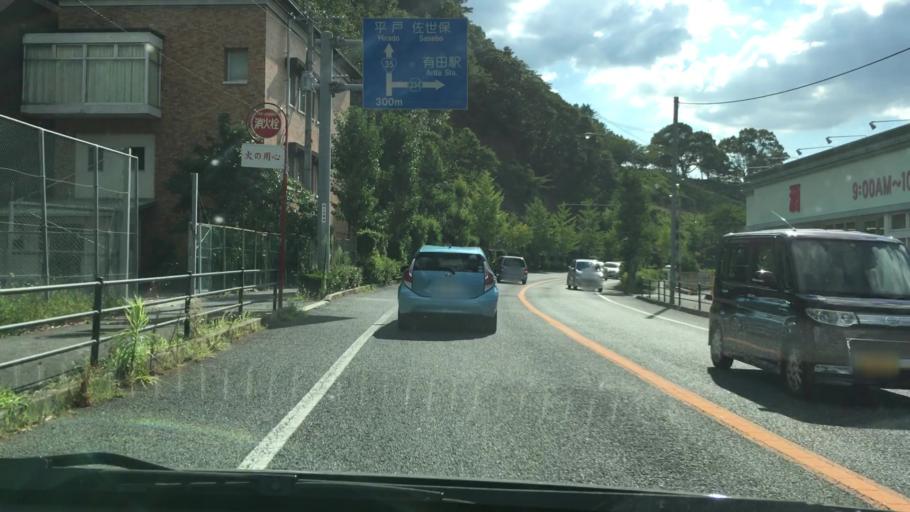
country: JP
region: Saga Prefecture
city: Imaricho-ko
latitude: 33.1802
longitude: 129.8834
